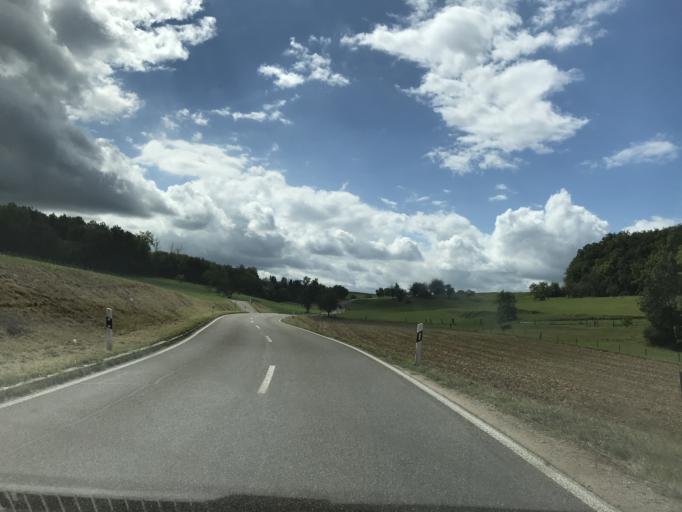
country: DE
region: Baden-Wuerttemberg
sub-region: Freiburg Region
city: Maulburg
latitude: 47.6264
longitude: 7.7698
